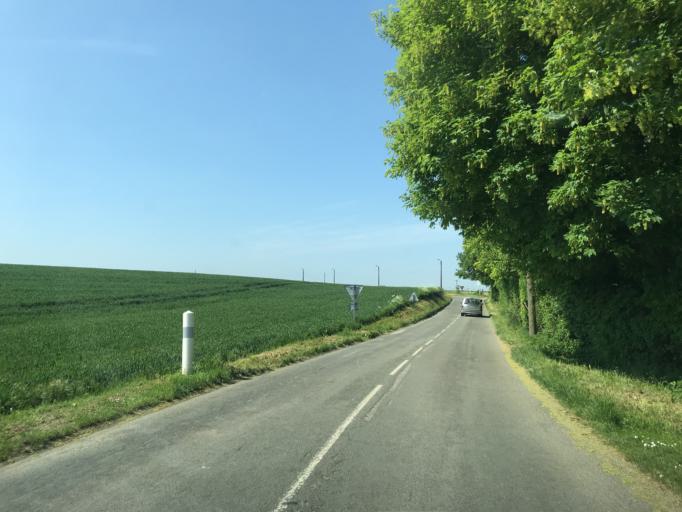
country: FR
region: Haute-Normandie
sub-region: Departement de la Seine-Maritime
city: Les Authieux-sur-le-Port-Saint-Ouen
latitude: 49.3516
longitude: 1.1482
